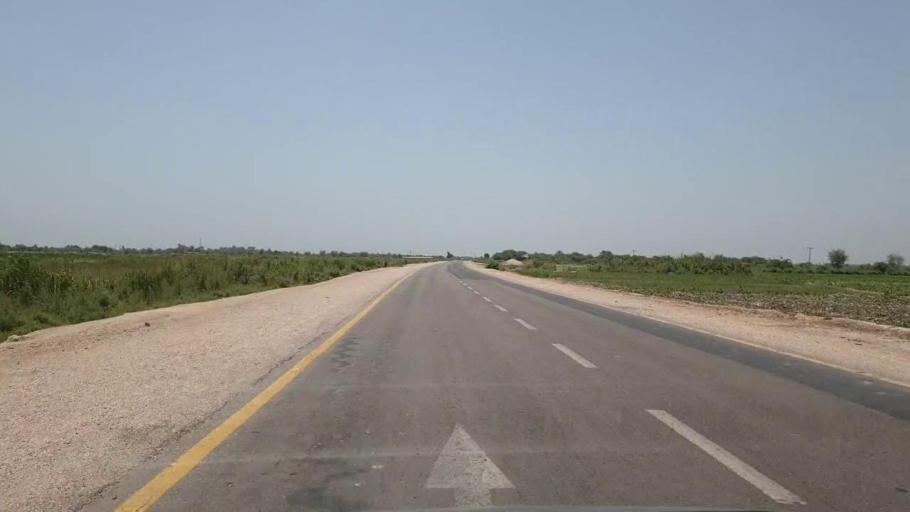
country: PK
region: Sindh
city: Sakrand
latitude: 26.1268
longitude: 68.3798
